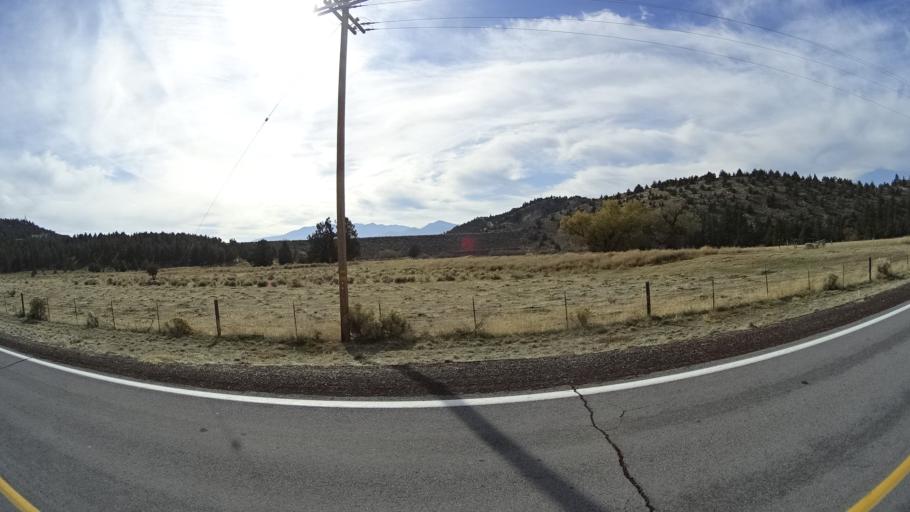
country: US
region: California
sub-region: Siskiyou County
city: Weed
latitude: 41.5450
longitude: -122.3731
